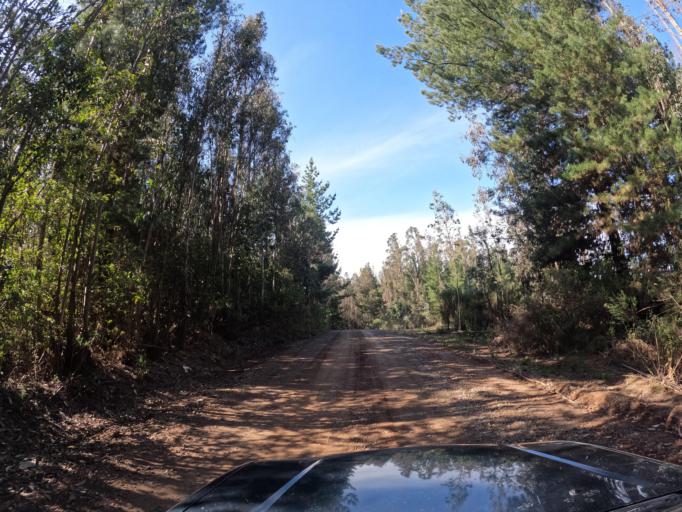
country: CL
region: Biobio
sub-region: Provincia de Biobio
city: La Laja
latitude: -37.0839
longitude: -72.7878
